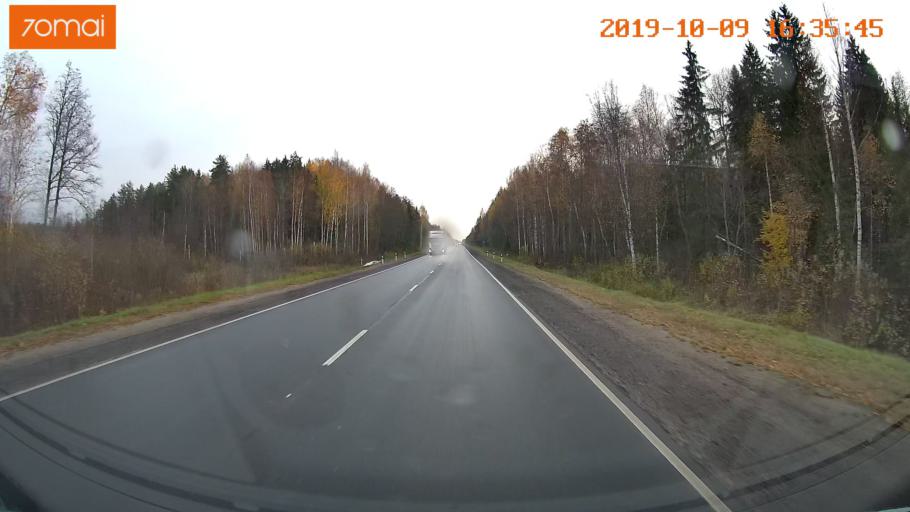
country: RU
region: Kostroma
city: Volgorechensk
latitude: 57.5513
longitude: 41.0045
